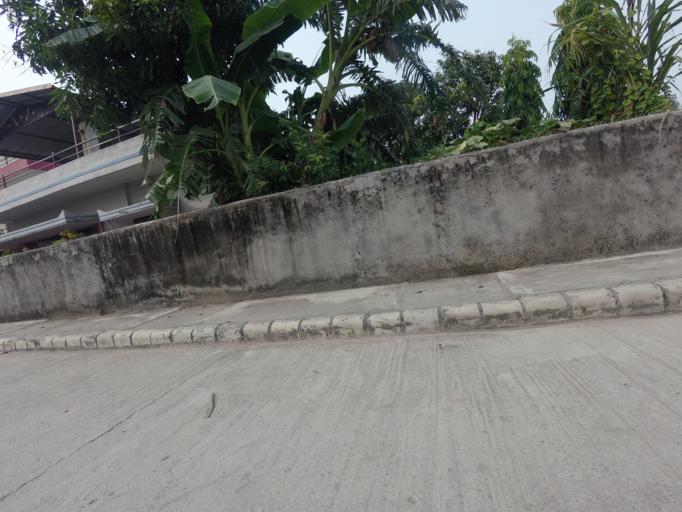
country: NP
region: Western Region
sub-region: Lumbini Zone
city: Bhairahawa
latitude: 27.5219
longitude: 83.4533
